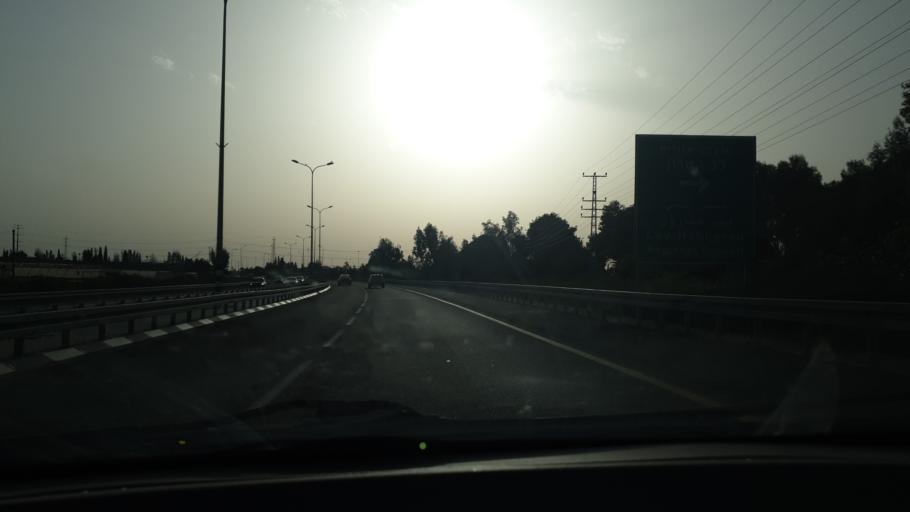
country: IL
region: Central District
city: Tel Mond
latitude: 32.2599
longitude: 34.9042
